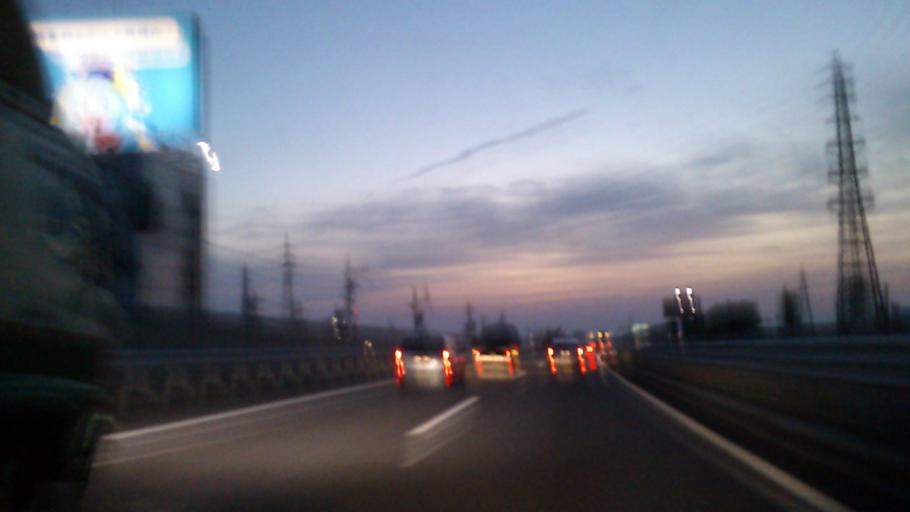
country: JP
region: Aichi
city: Komaki
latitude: 35.2981
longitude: 136.9254
